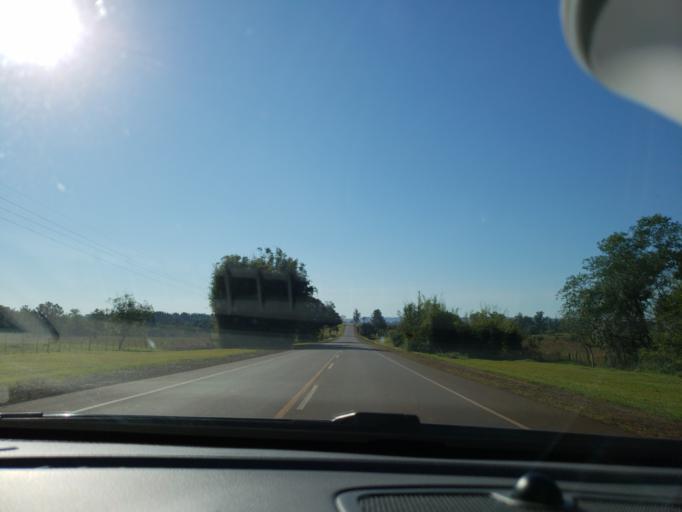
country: AR
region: Misiones
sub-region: Departamento de Apostoles
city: San Jose
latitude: -27.7953
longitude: -55.7711
